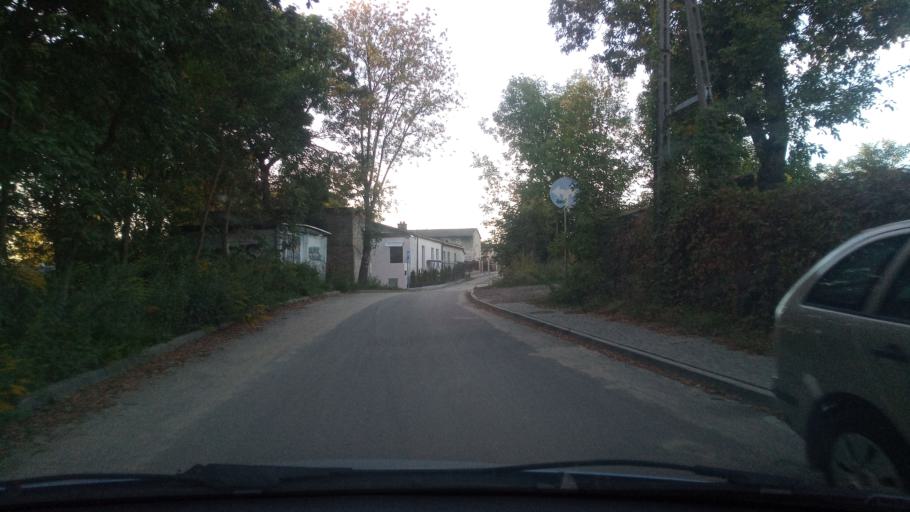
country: PL
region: Silesian Voivodeship
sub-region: Powiat bedzinski
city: Czeladz
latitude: 50.2870
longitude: 19.0753
